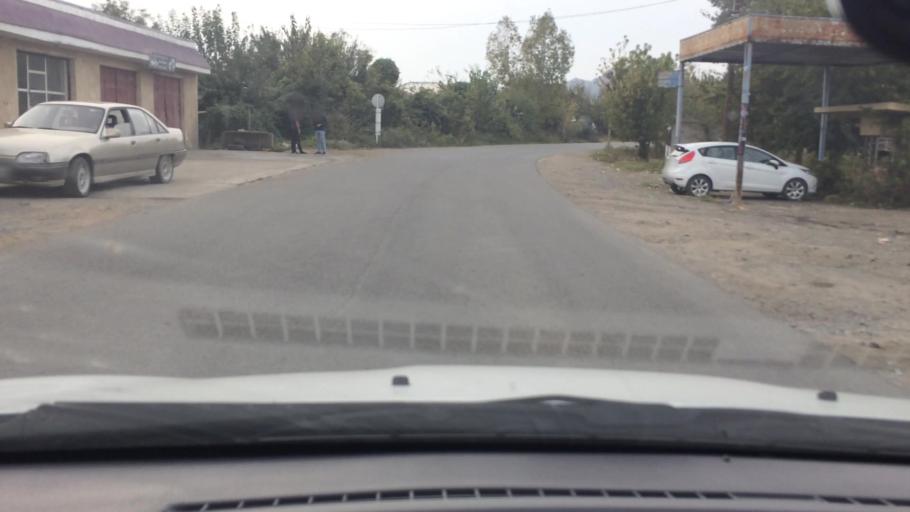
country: GE
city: Naghvarevi
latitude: 41.3541
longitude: 44.8607
